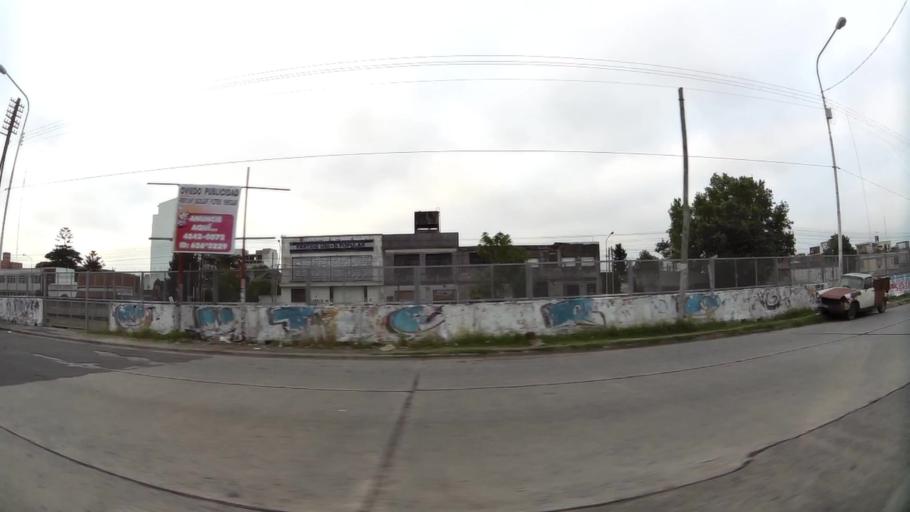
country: AR
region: Buenos Aires
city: San Justo
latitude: -34.6396
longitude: -58.5370
